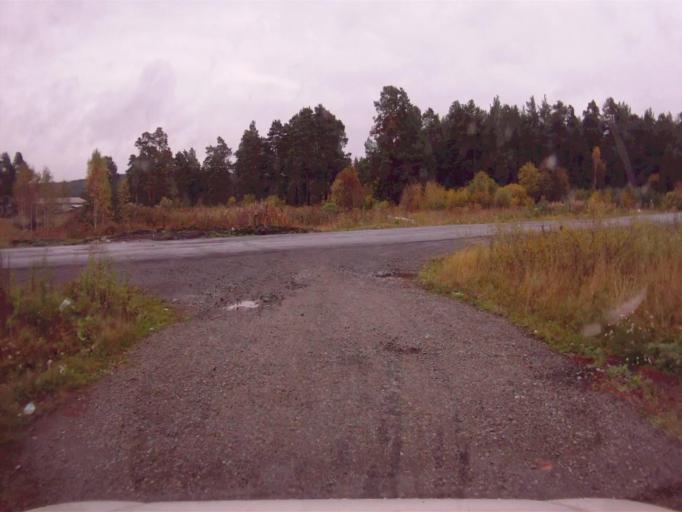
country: RU
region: Chelyabinsk
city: Verkhniy Ufaley
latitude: 56.0541
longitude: 60.1730
